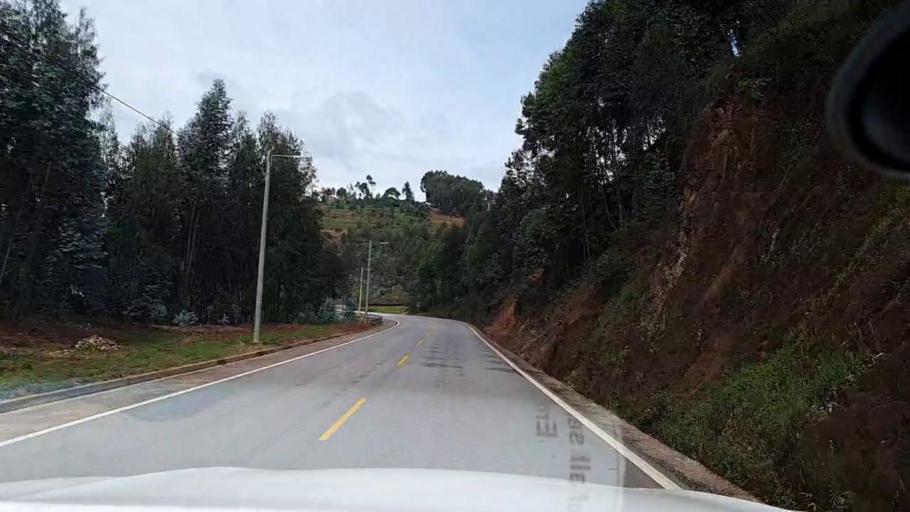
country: RW
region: Southern Province
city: Nzega
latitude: -2.5144
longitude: 29.4620
